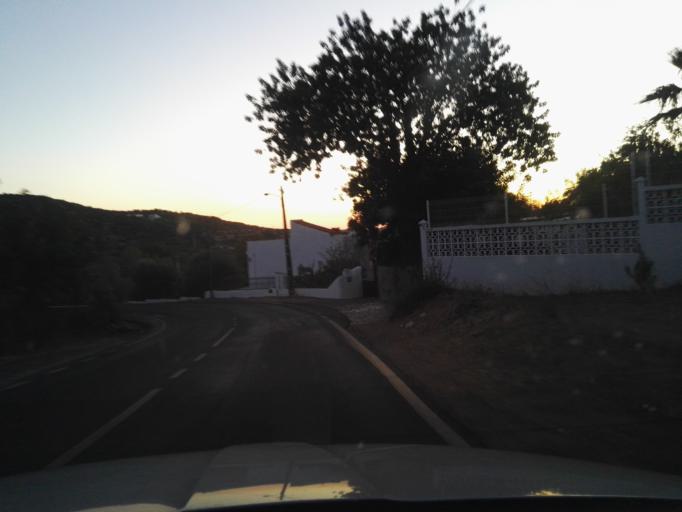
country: PT
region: Faro
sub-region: Sao Bras de Alportel
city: Sao Bras de Alportel
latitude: 37.1528
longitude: -7.9322
